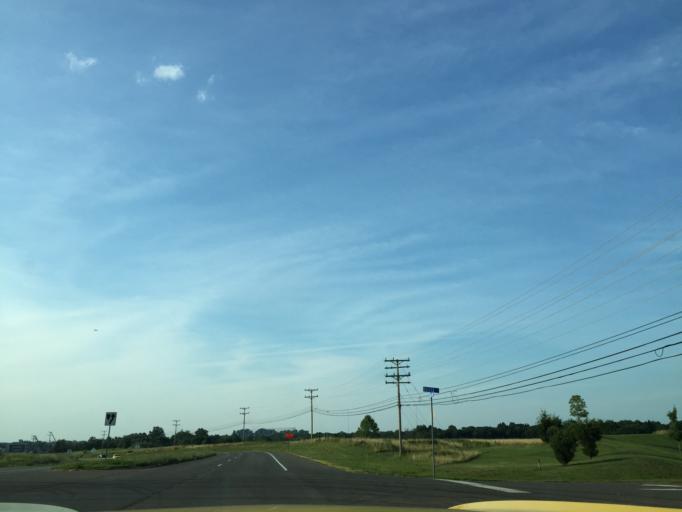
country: US
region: Virginia
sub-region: Loudoun County
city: University Center
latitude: 39.0334
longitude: -77.4476
